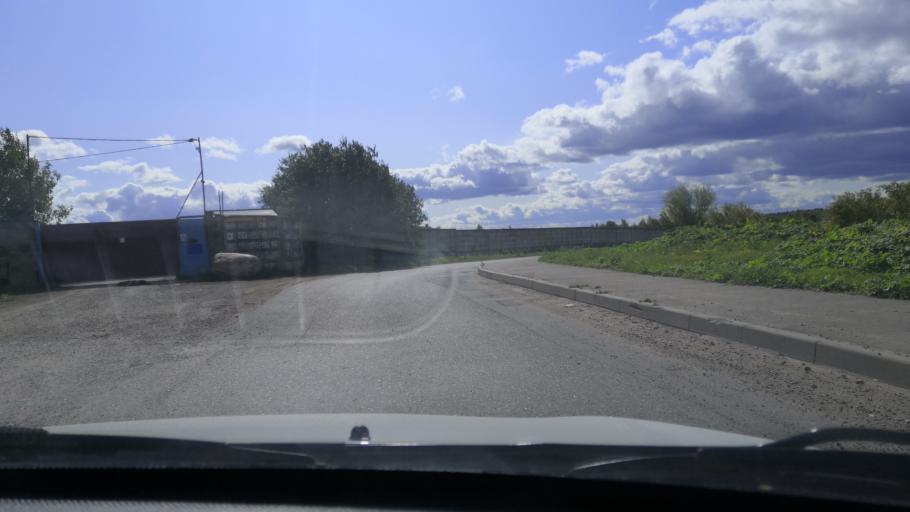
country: RU
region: Moskovskaya
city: Povarovo
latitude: 56.0687
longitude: 37.0511
